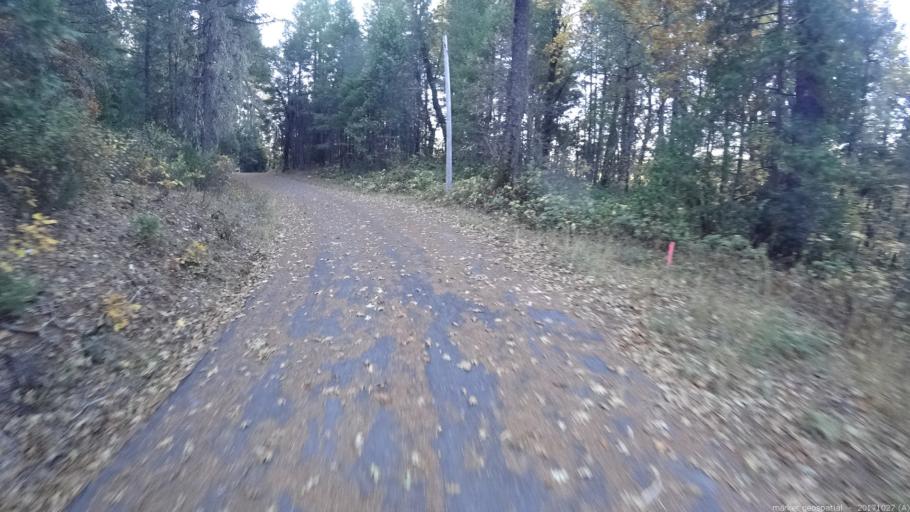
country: US
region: California
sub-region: Shasta County
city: Burney
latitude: 41.0264
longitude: -121.9025
